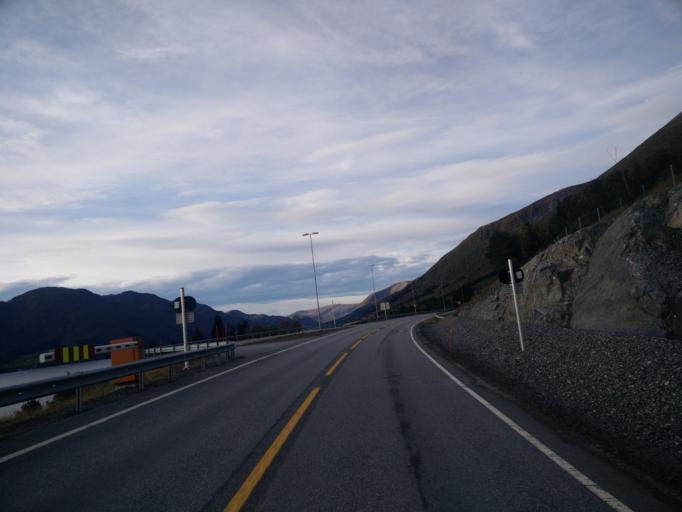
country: NO
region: More og Romsdal
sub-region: Gjemnes
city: Batnfjordsora
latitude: 62.9537
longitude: 7.7687
